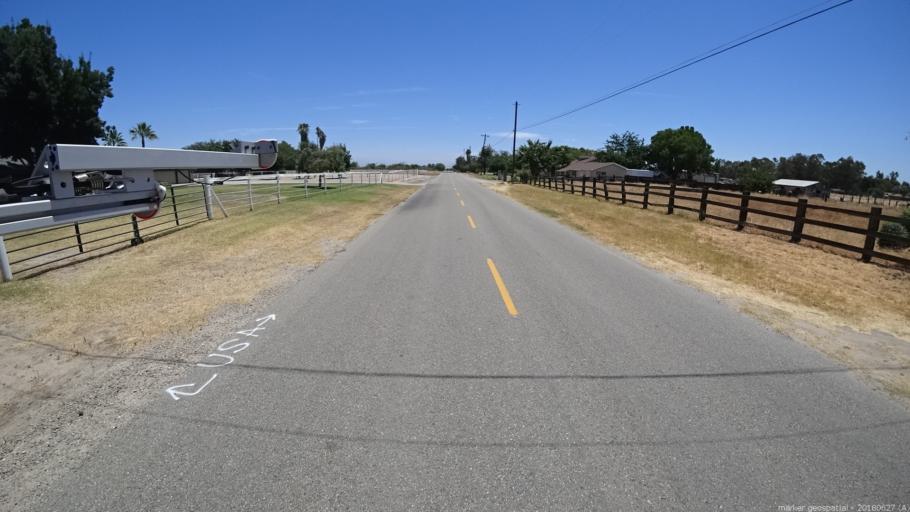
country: US
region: California
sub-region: Madera County
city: Bonadelle Ranchos-Madera Ranchos
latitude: 36.9448
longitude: -119.9008
